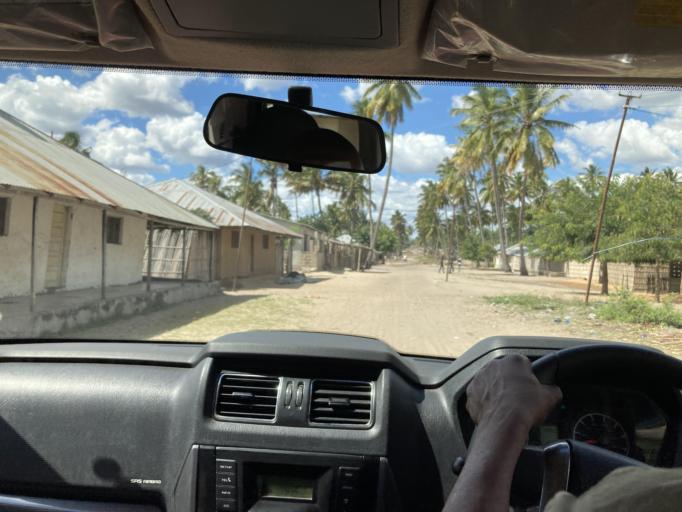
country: MZ
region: Cabo Delgado
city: Montepuez
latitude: -13.1304
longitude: 39.0084
